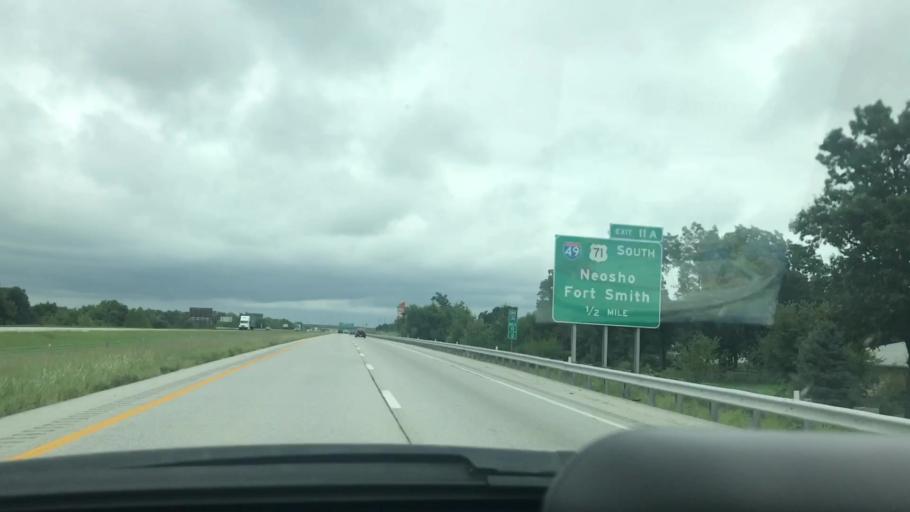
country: US
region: Missouri
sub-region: Jasper County
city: Duquesne
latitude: 37.0572
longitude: -94.4400
